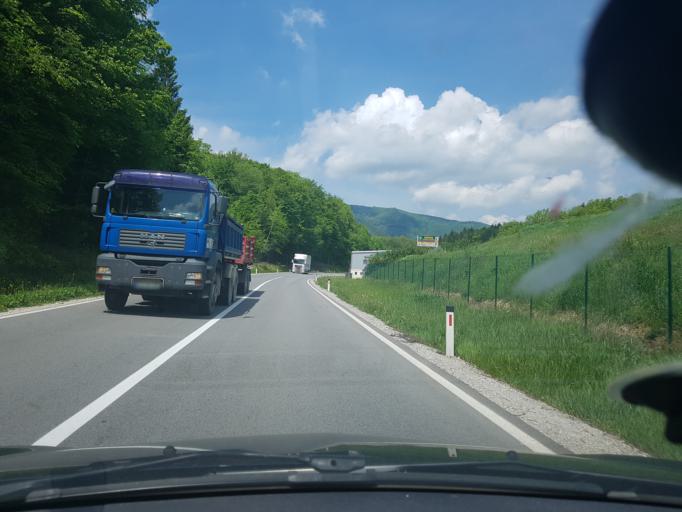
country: SI
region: Rogatec
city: Rogatec
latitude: 46.2349
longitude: 15.6722
